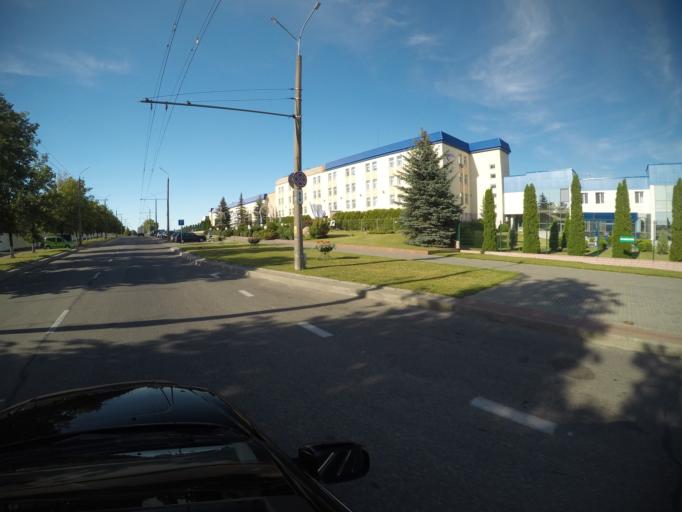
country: BY
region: Grodnenskaya
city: Hrodna
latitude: 53.7084
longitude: 23.8278
